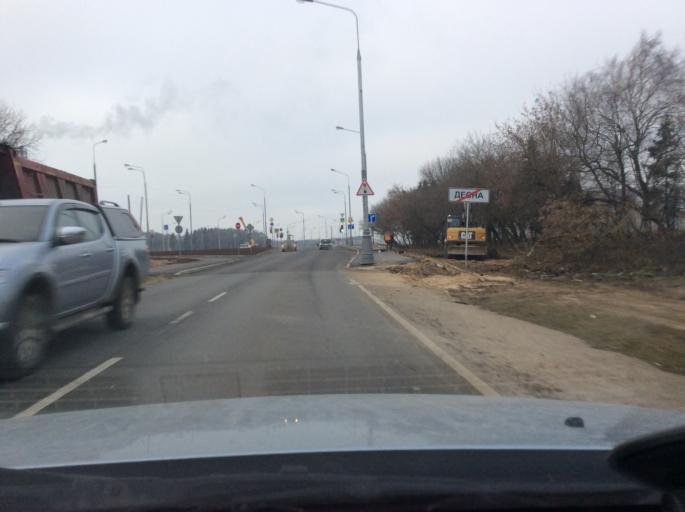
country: RU
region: Moskovskaya
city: Vatutinki
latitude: 55.5179
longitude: 37.3680
